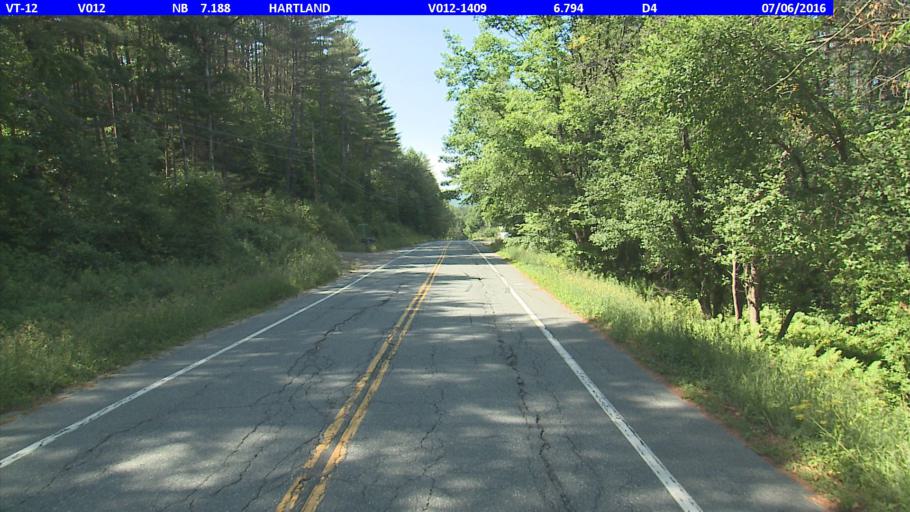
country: US
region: Vermont
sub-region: Windsor County
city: Woodstock
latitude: 43.6140
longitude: -72.4554
